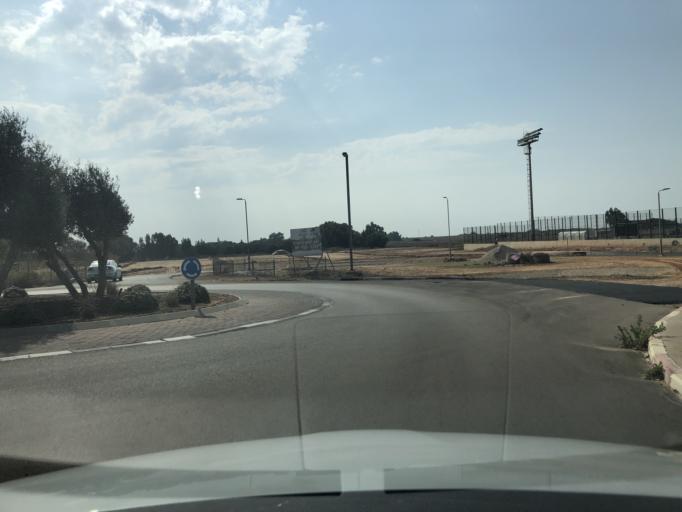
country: IL
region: Tel Aviv
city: Kefar Shemaryahu
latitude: 32.2134
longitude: 34.8227
